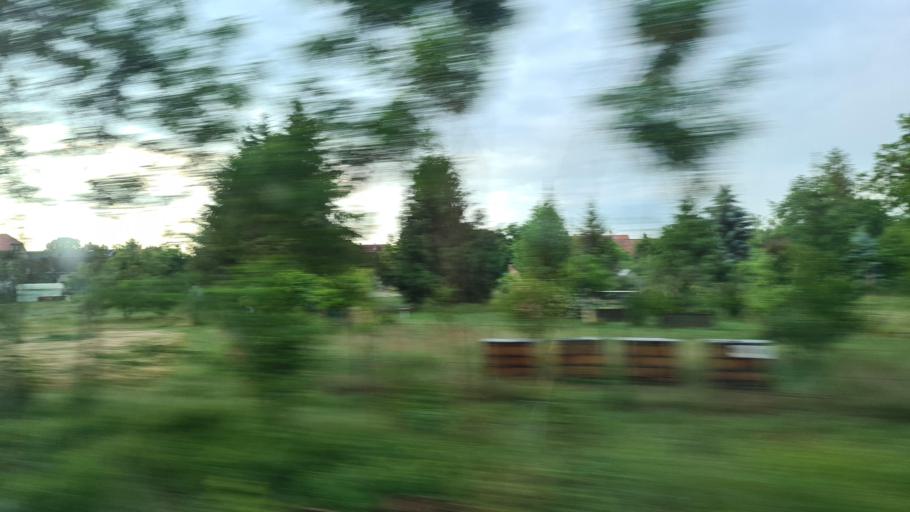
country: DE
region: Brandenburg
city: Schonborn
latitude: 51.6026
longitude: 13.4898
